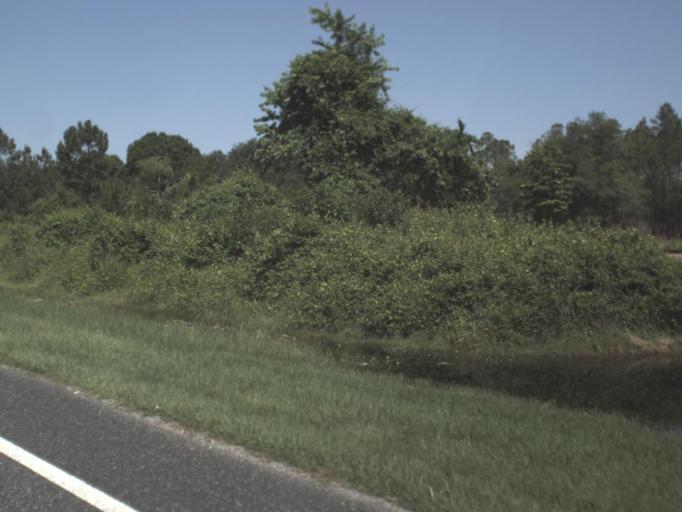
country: US
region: Florida
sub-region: Columbia County
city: Watertown
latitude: 30.2028
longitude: -82.4459
